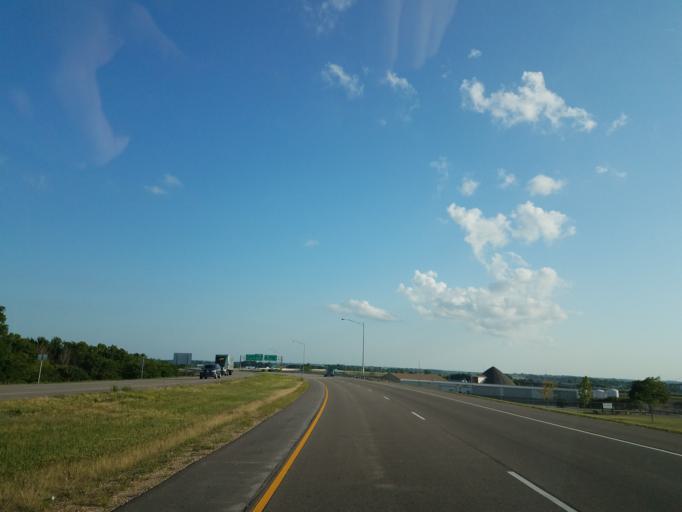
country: US
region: Illinois
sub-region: McLean County
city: Bloomington
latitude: 40.4486
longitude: -89.0159
